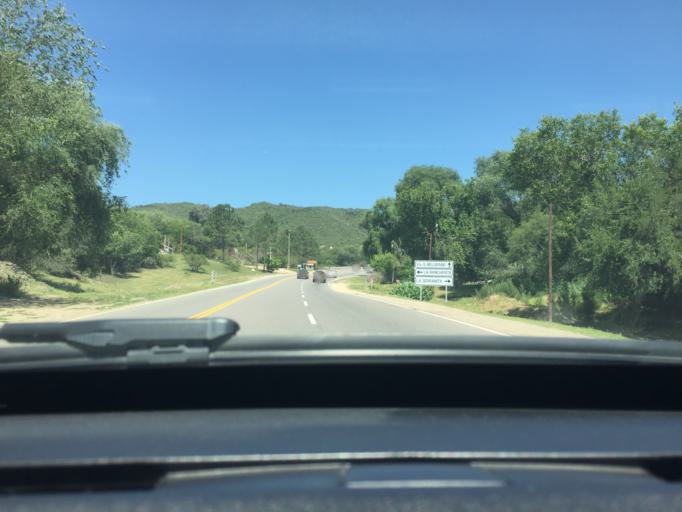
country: AR
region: Cordoba
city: Alta Gracia
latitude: -31.7412
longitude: -64.4561
